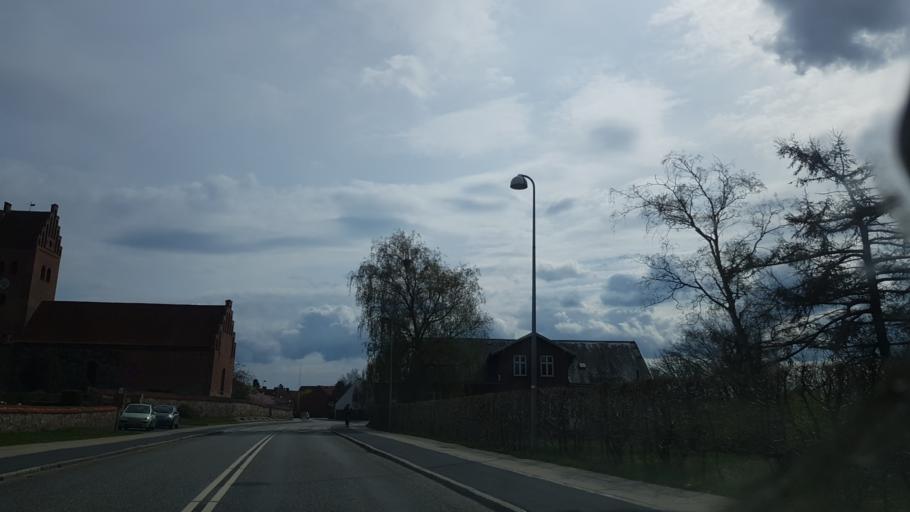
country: DK
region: Capital Region
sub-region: Allerod Kommune
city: Lillerod
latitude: 55.8743
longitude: 12.3458
